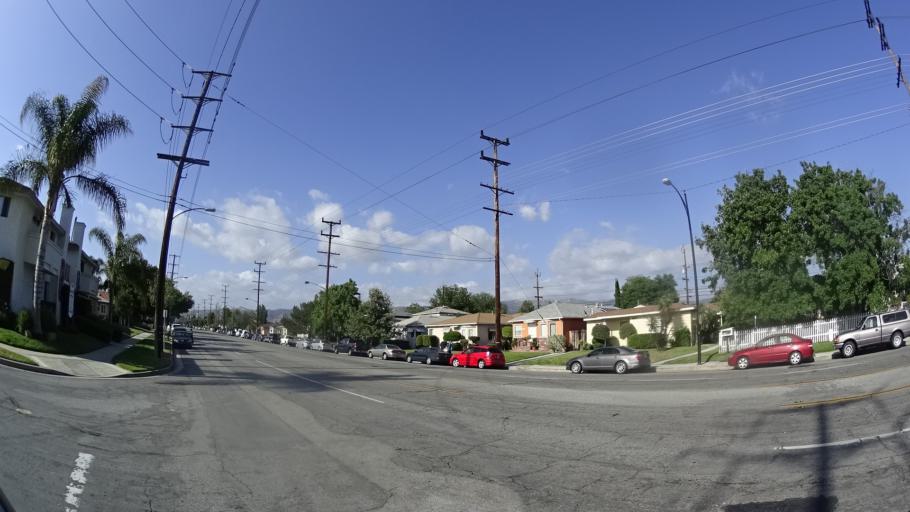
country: US
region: California
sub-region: Los Angeles County
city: North Hollywood
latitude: 34.1774
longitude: -118.3494
